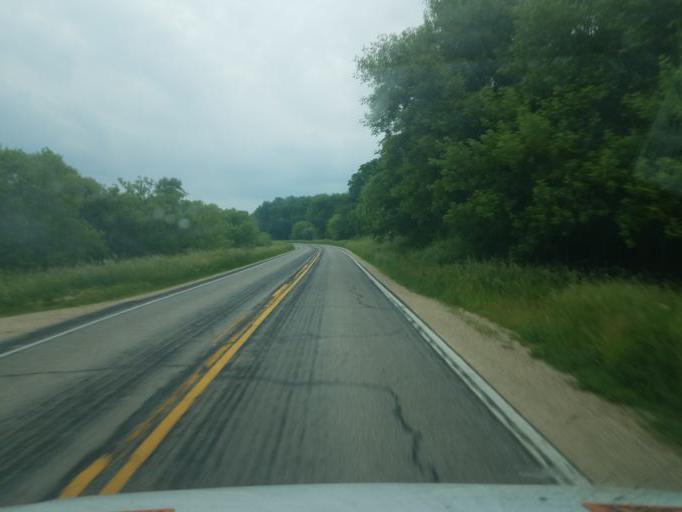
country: US
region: Wisconsin
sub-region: Vernon County
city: Hillsboro
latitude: 43.6448
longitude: -90.4181
